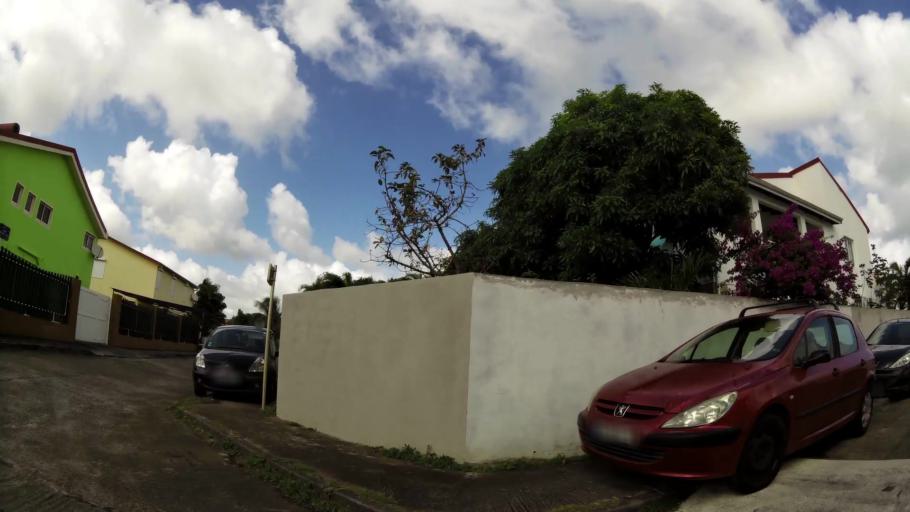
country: MQ
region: Martinique
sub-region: Martinique
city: Le Lamentin
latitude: 14.6129
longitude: -60.9871
